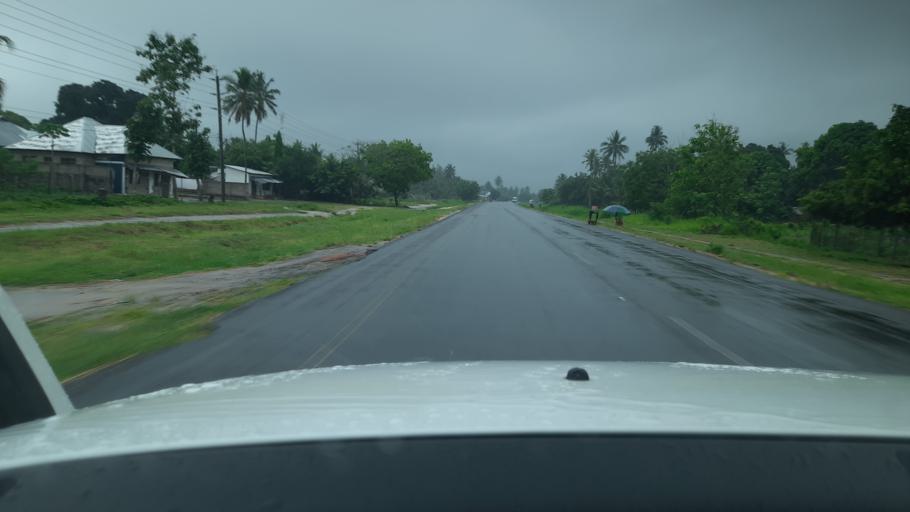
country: TZ
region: Pwani
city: Bagamoyo
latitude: -6.5358
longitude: 38.9892
